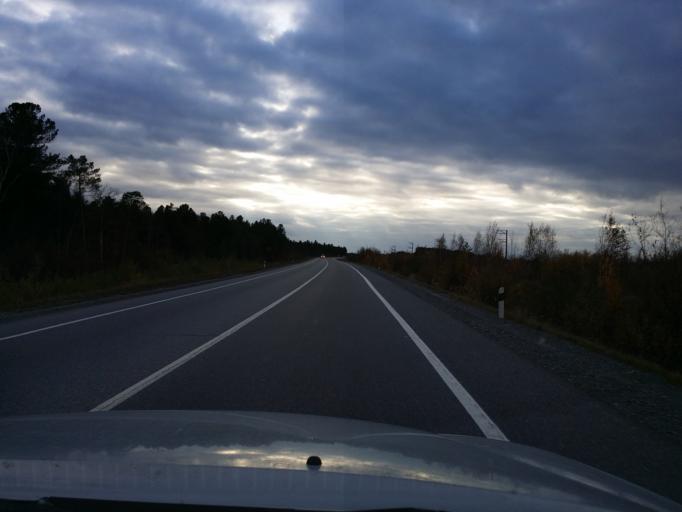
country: RU
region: Khanty-Mansiyskiy Avtonomnyy Okrug
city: Surgut
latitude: 61.4236
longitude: 73.8808
